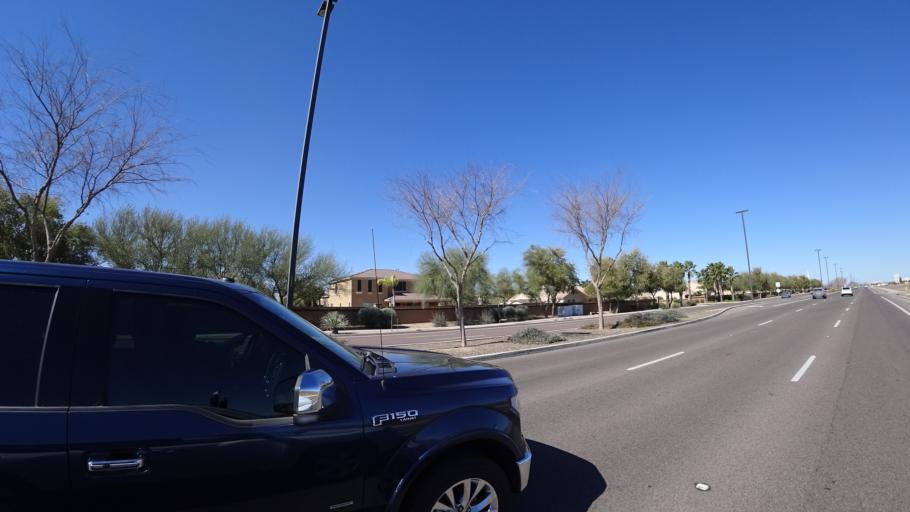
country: US
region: Arizona
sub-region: Maricopa County
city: Gilbert
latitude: 33.2669
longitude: -111.7552
